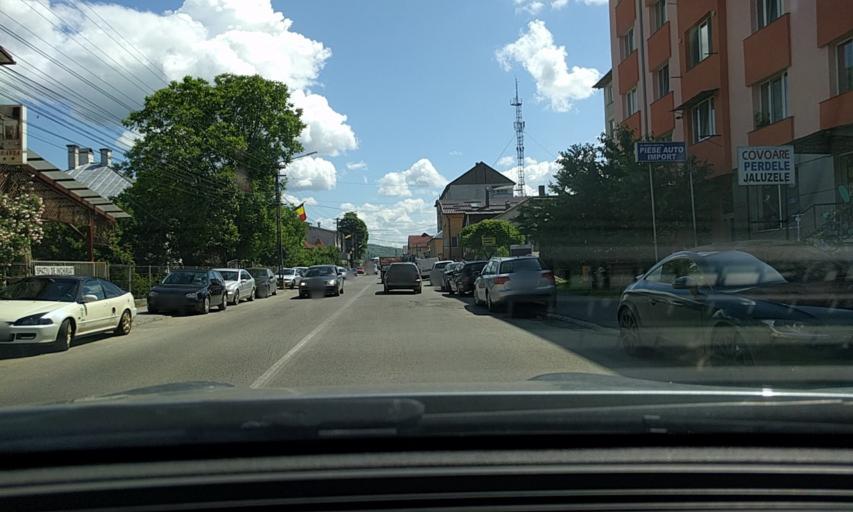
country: RO
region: Bistrita-Nasaud
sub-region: Oras Nasaud
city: Nasaud
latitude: 47.2838
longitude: 24.4167
